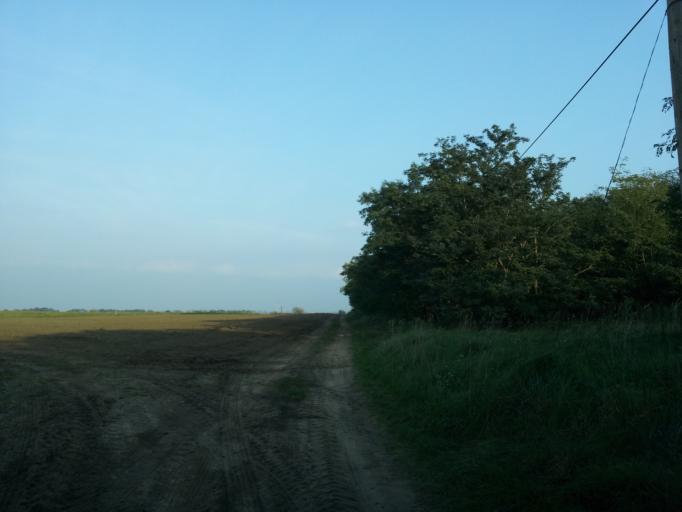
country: HU
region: Komarom-Esztergom
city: Kisber
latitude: 47.5122
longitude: 18.0124
